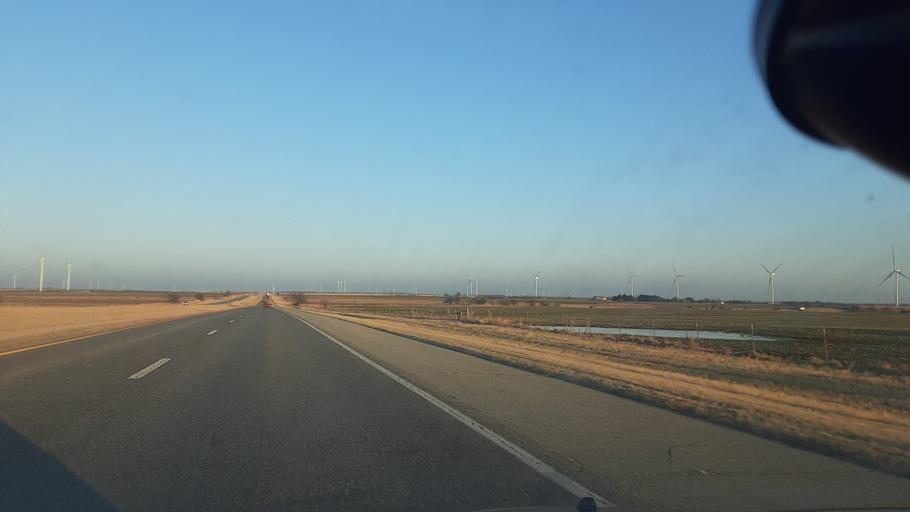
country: US
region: Oklahoma
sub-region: Noble County
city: Perry
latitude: 36.3975
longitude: -97.5102
